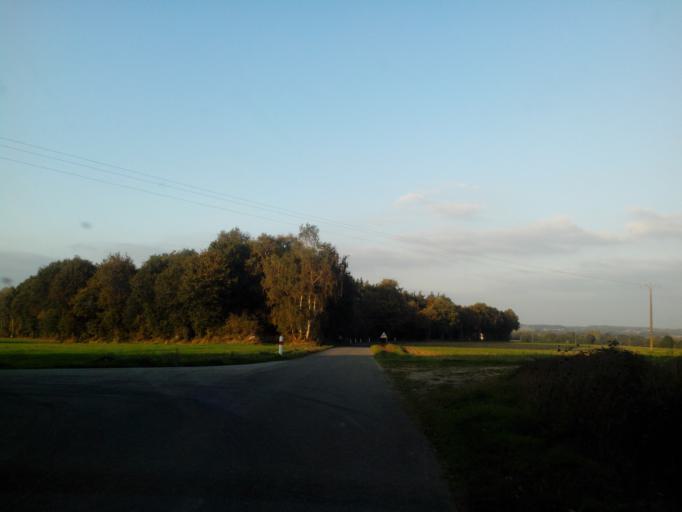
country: FR
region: Brittany
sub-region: Departement du Morbihan
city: Guilliers
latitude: 48.1087
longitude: -2.3974
